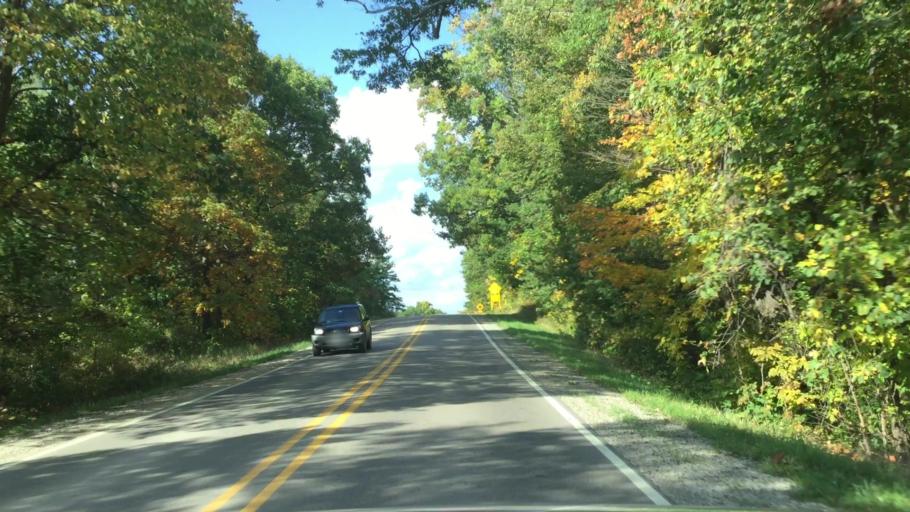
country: US
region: Michigan
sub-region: Oakland County
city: Milford
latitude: 42.6609
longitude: -83.7011
